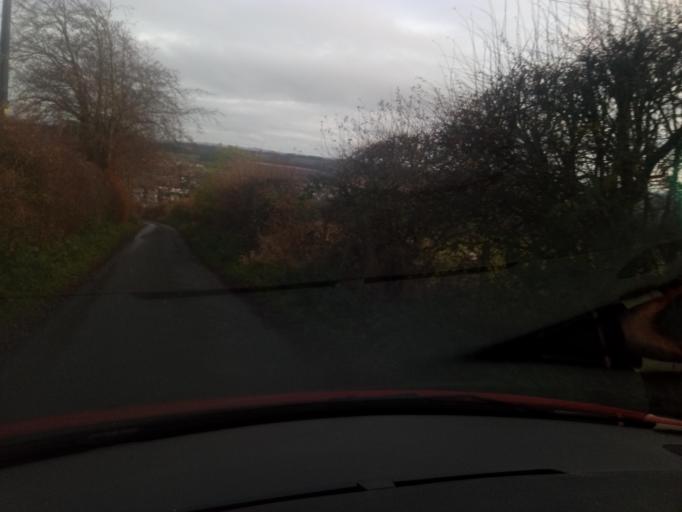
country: GB
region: Scotland
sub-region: The Scottish Borders
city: Jedburgh
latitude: 55.4791
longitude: -2.5657
